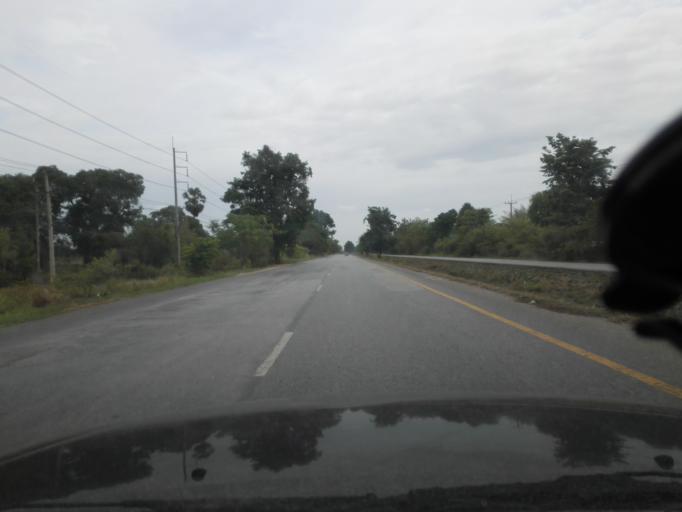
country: TH
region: Kamphaeng Phet
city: Khlong Khlung
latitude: 16.1193
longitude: 99.7195
